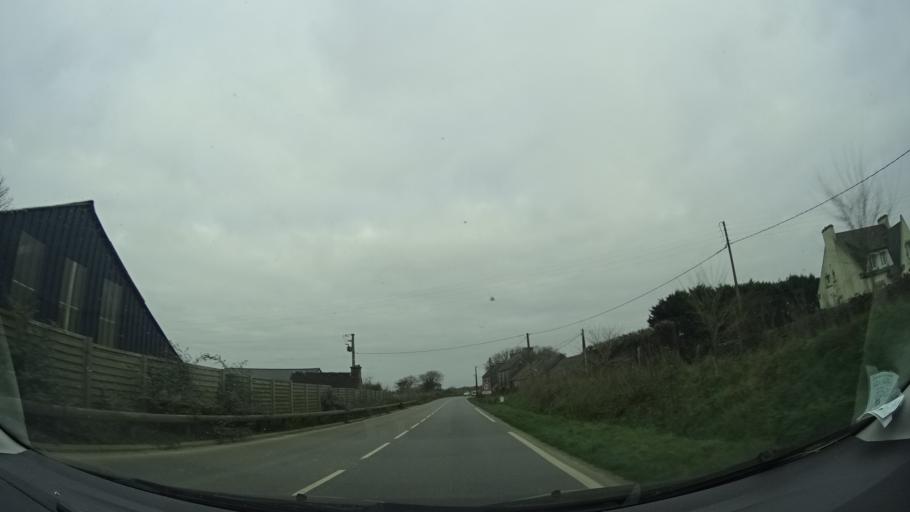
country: FR
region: Brittany
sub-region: Departement du Finistere
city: Guilers
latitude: 48.4487
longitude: -4.5470
